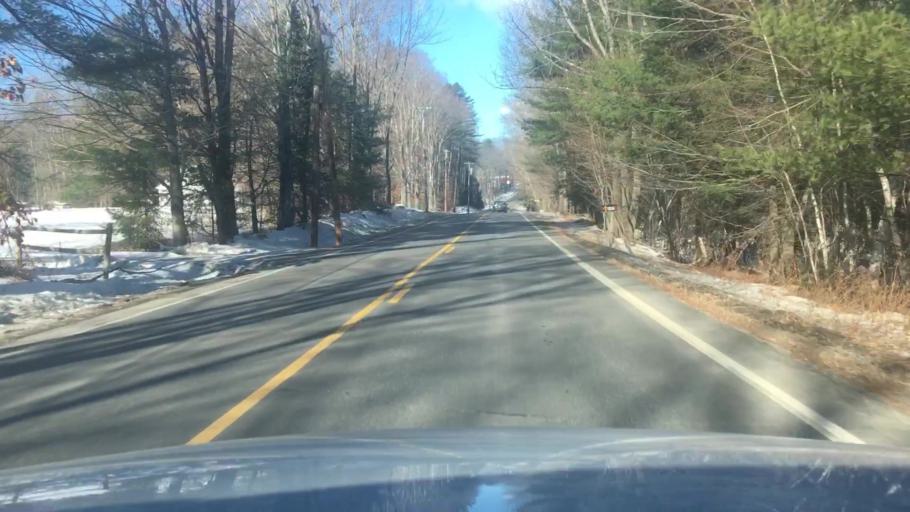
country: US
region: Maine
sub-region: Somerset County
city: Skowhegan
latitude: 44.7289
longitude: -69.6783
